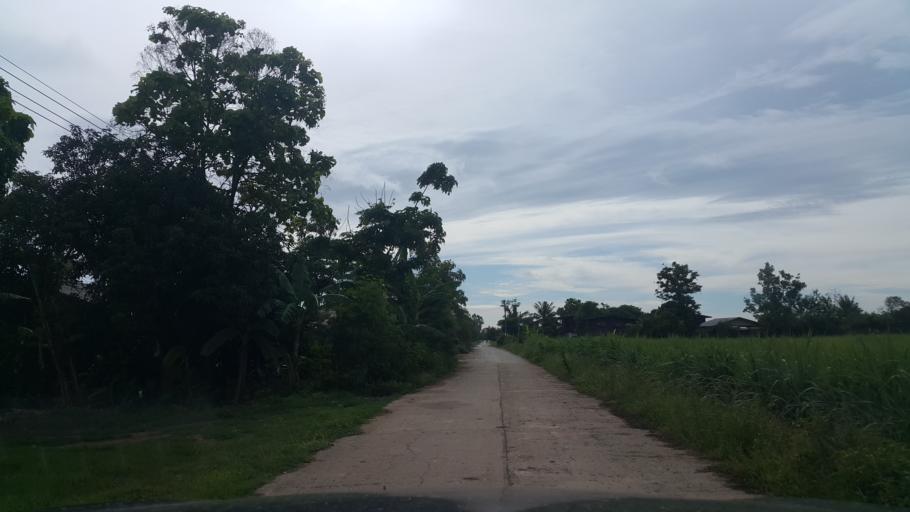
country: TH
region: Sukhothai
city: Sawankhalok
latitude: 17.2672
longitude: 99.9198
